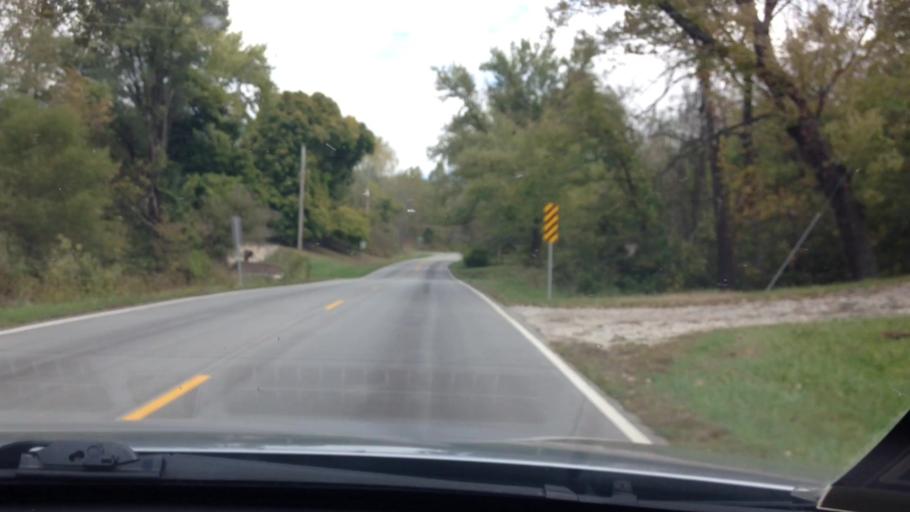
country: US
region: Missouri
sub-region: Platte County
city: Weatherby Lake
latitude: 39.2464
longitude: -94.7961
